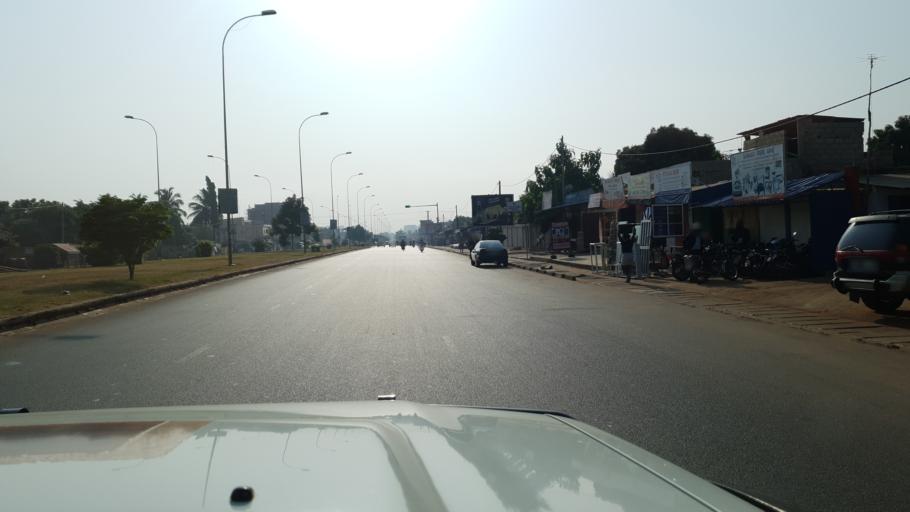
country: TG
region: Maritime
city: Lome
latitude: 6.2010
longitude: 1.1951
